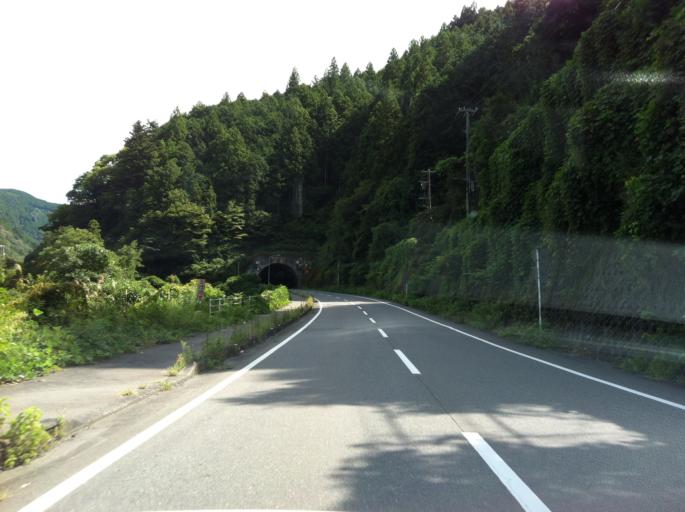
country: JP
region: Shizuoka
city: Kanaya
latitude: 35.0560
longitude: 138.0881
